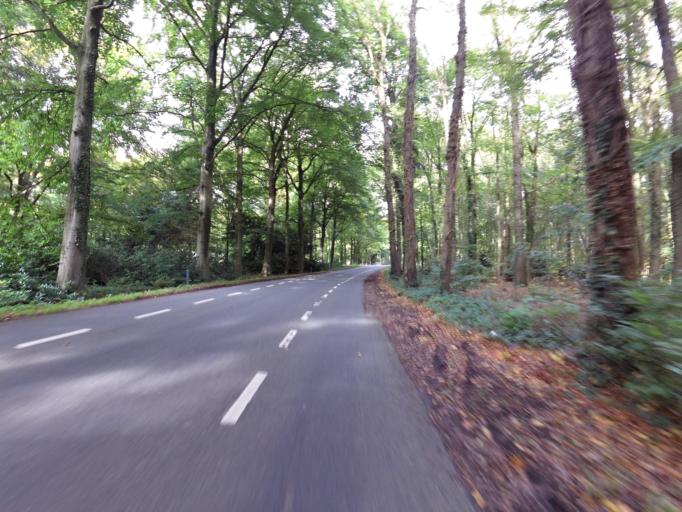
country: NL
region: Gelderland
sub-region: Gemeente Bronckhorst
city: Baak
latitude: 52.0941
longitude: 6.2523
